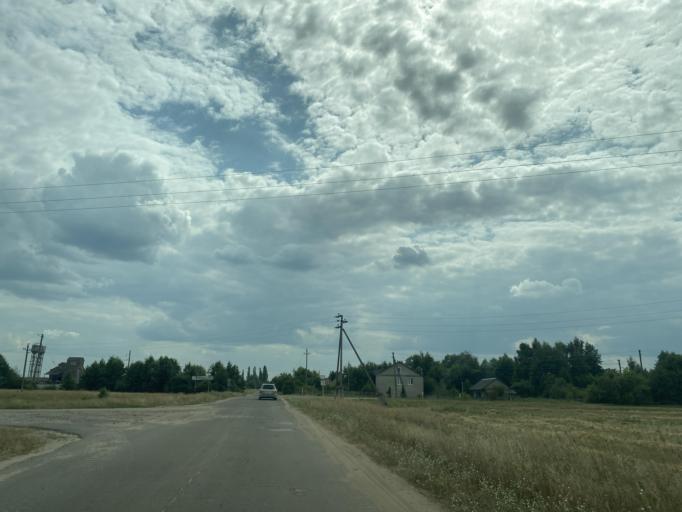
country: BY
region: Brest
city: Ivanava
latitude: 52.3533
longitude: 25.6296
